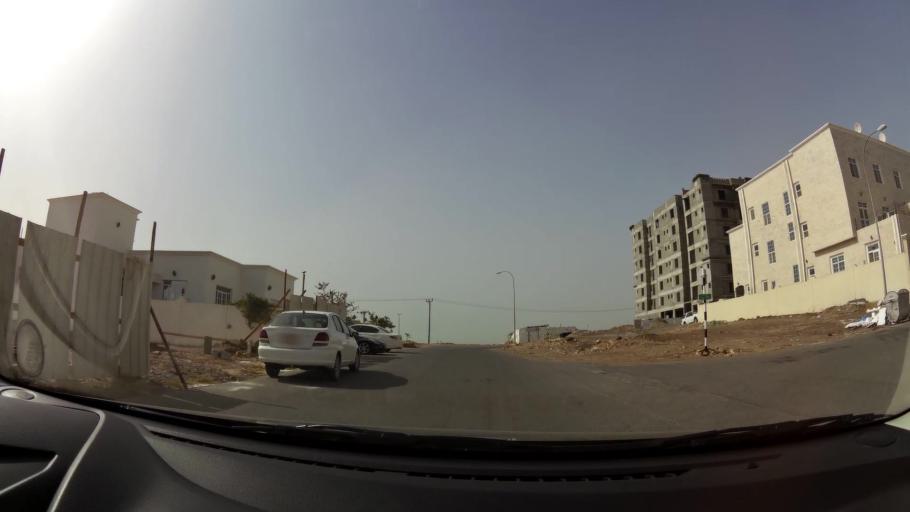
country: OM
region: Muhafazat Masqat
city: Bawshar
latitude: 23.5641
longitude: 58.3627
